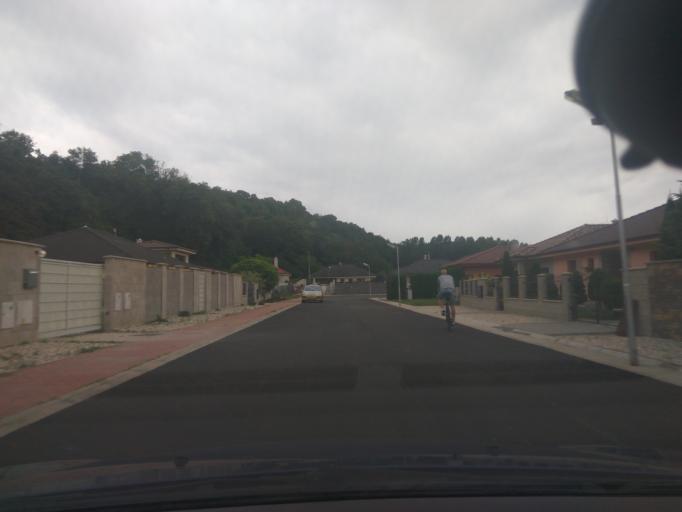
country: SK
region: Trenciansky
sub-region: Okres Nove Mesto nad Vahom
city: Nove Mesto nad Vahom
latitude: 48.6939
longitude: 17.8819
